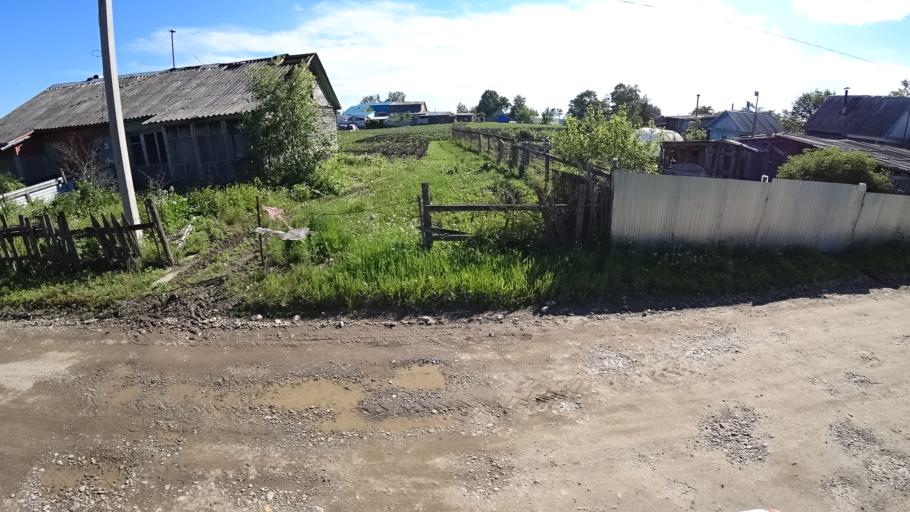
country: RU
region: Khabarovsk Krai
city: Khor
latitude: 47.8902
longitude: 134.9923
